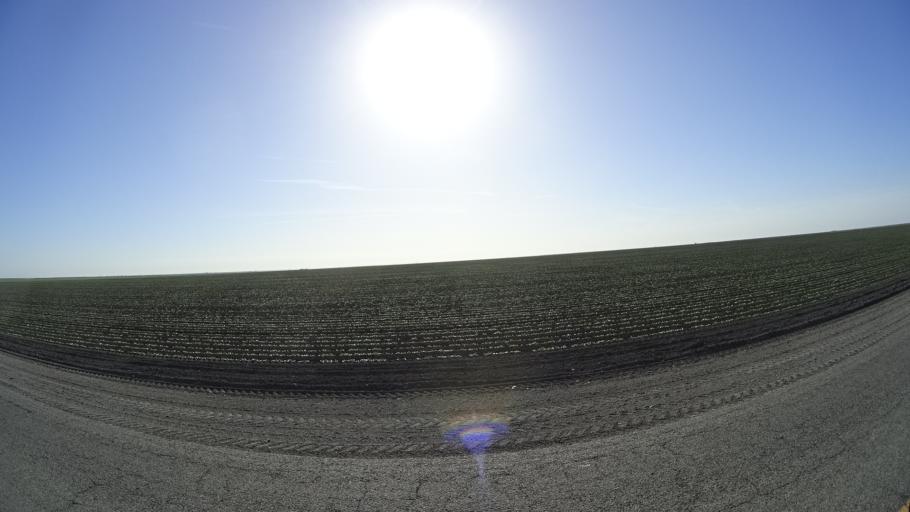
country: US
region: California
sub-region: Kings County
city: Stratford
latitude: 36.0991
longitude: -119.7979
